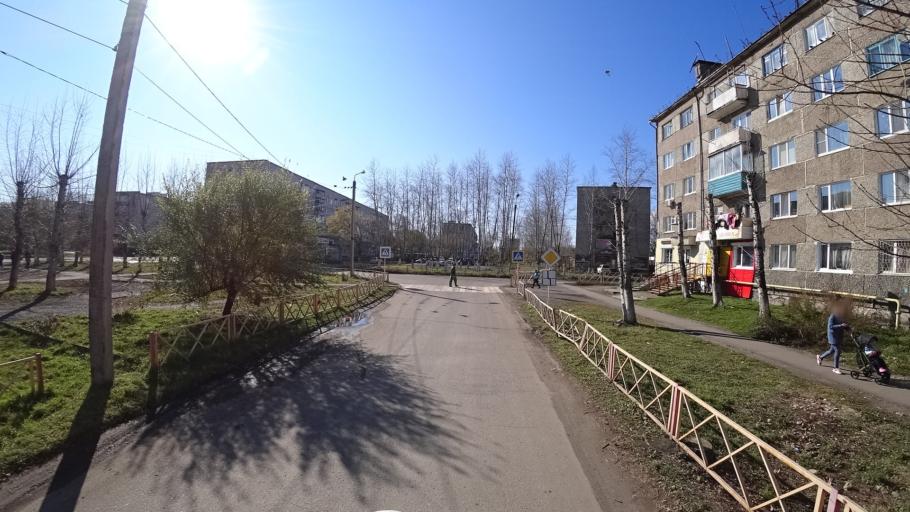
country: RU
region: Khabarovsk Krai
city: Amursk
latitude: 50.0992
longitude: 136.5126
